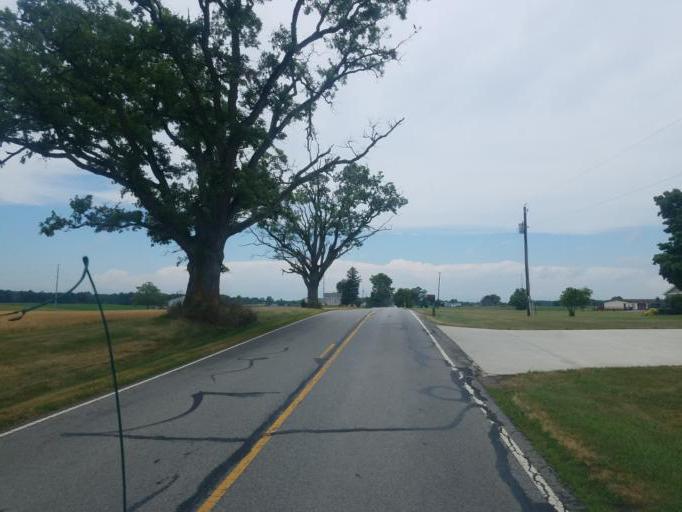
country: US
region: Indiana
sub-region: DeKalb County
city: Butler
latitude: 41.3861
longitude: -84.8552
